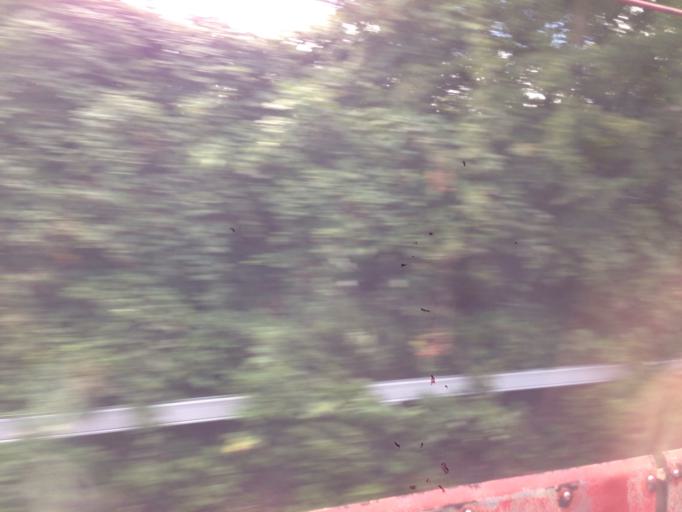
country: DE
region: Schleswig-Holstein
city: Sylt-Ost
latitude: 54.8718
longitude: 8.4399
